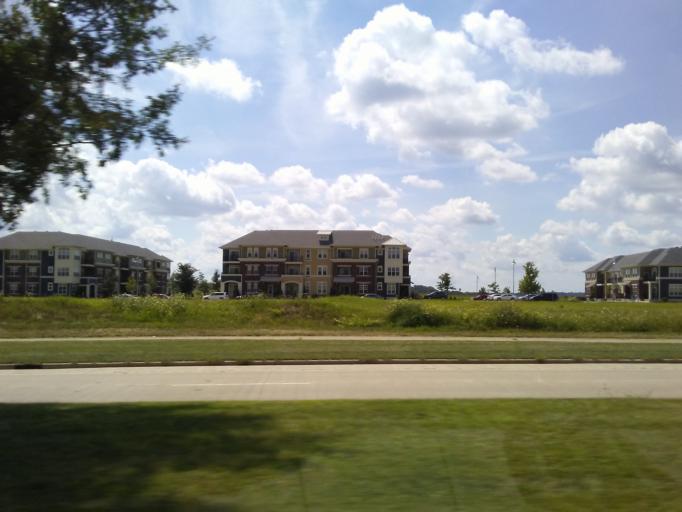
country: US
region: Wisconsin
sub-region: Dane County
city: Verona
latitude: 42.9878
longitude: -89.5547
